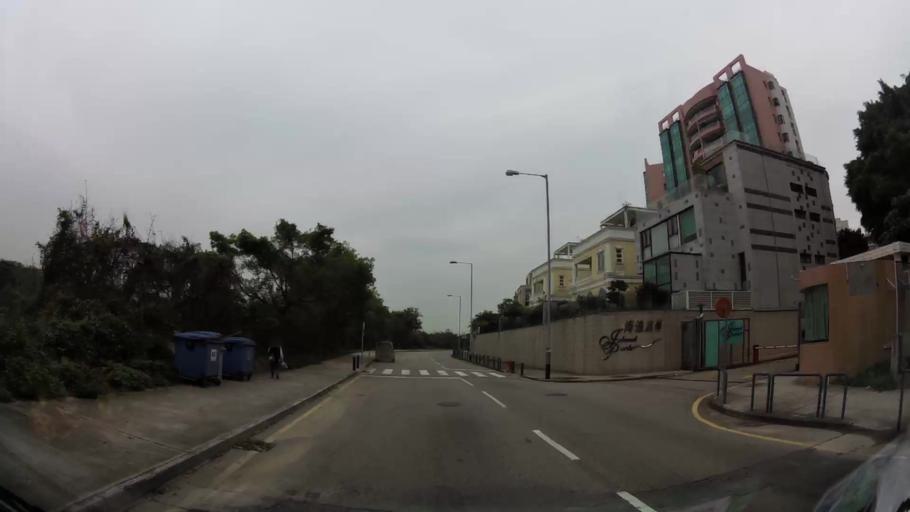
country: MO
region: Macau
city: Macau
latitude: 22.1645
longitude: 113.5558
